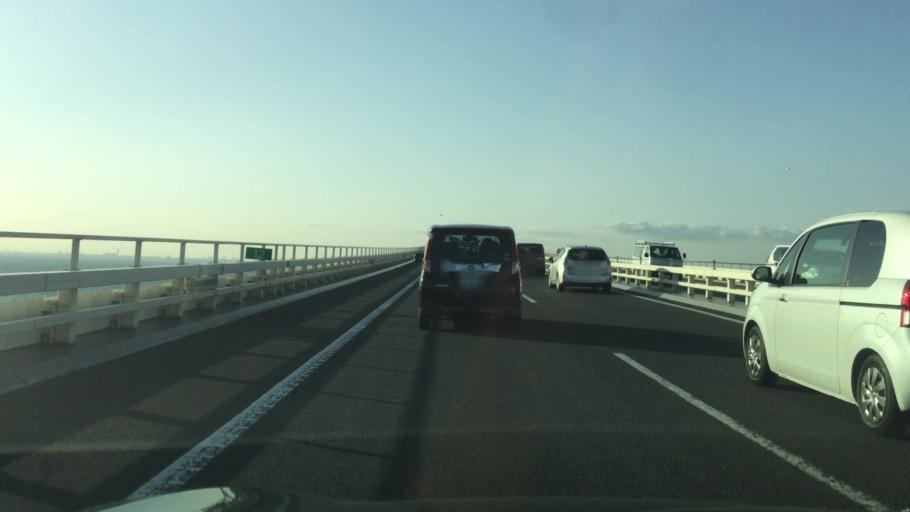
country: JP
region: Chiba
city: Kisarazu
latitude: 35.4507
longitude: 139.8944
